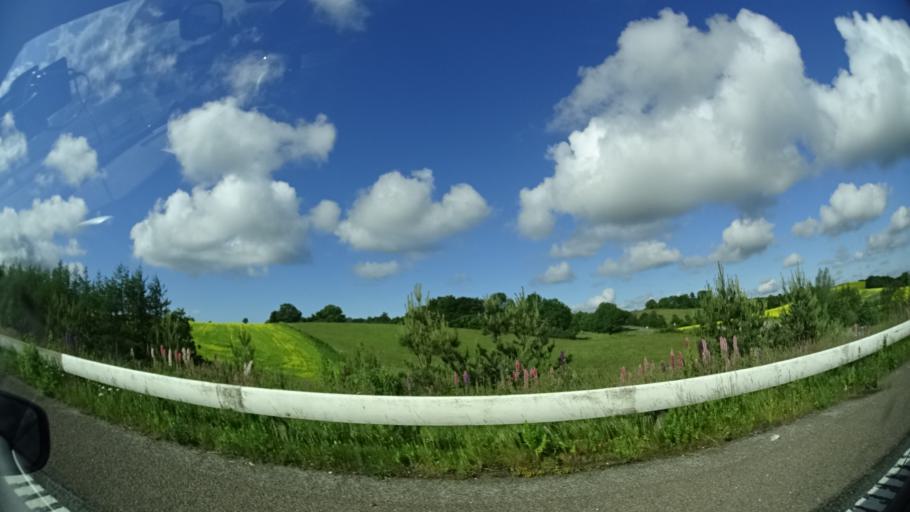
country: DK
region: Central Jutland
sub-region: Syddjurs Kommune
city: Ronde
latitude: 56.3030
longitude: 10.5067
